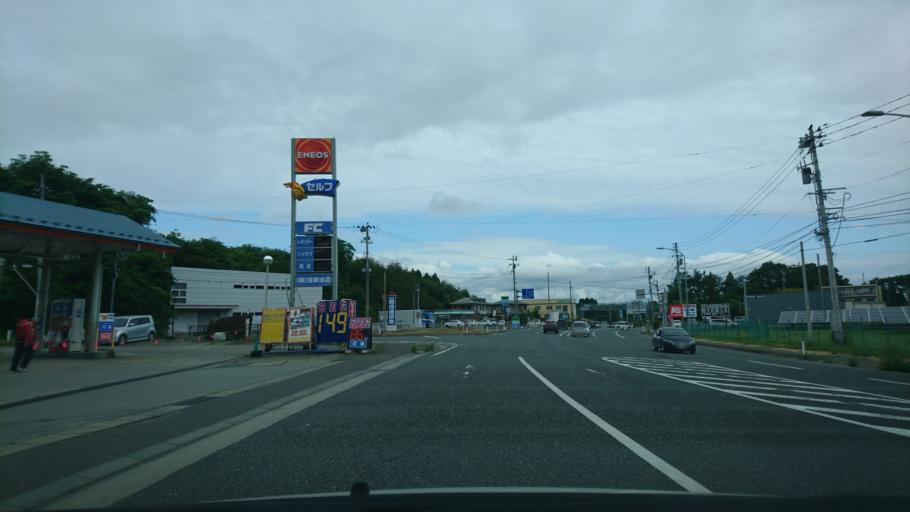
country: JP
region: Iwate
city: Ichinoseki
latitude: 38.9095
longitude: 141.1614
